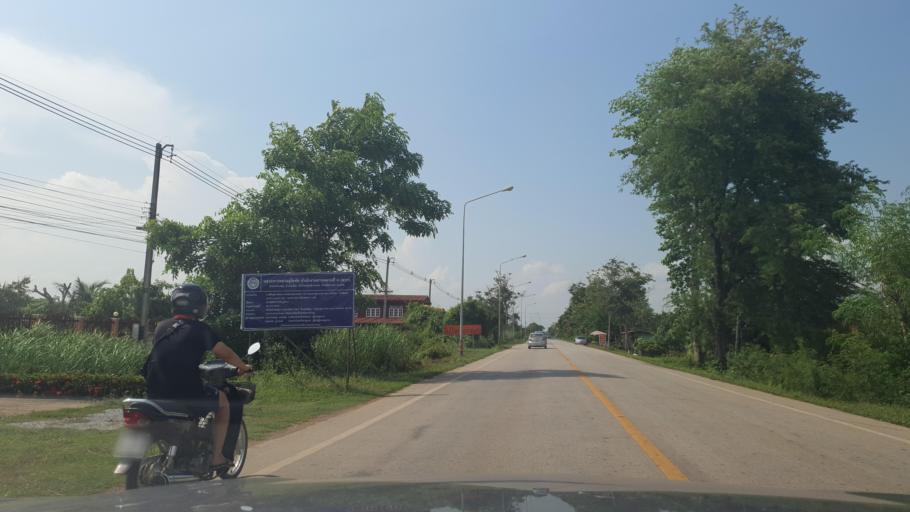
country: TH
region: Sukhothai
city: Si Samrong
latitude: 17.2003
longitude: 99.8487
